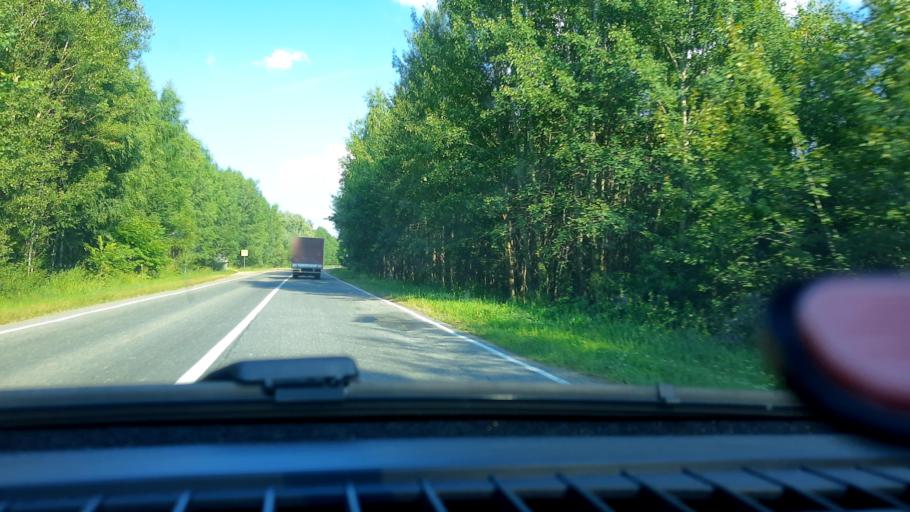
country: RU
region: Nizjnij Novgorod
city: Neklyudovo
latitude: 56.5167
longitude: 43.9245
